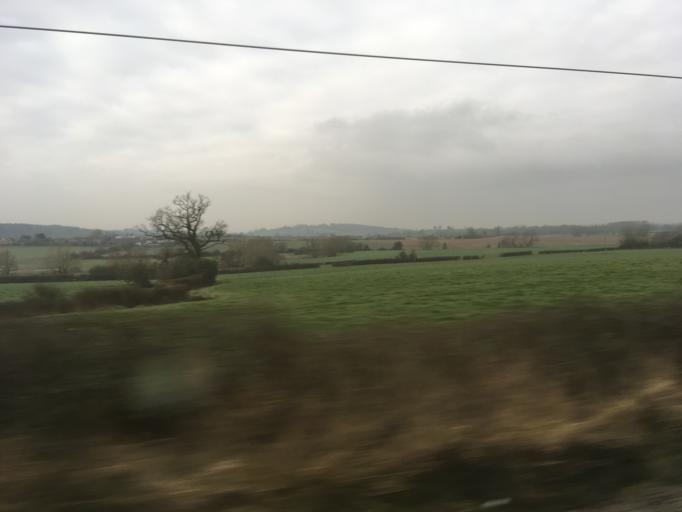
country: GB
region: England
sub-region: Wiltshire
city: Royal Wootton Bassett
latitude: 51.5439
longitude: -1.9217
